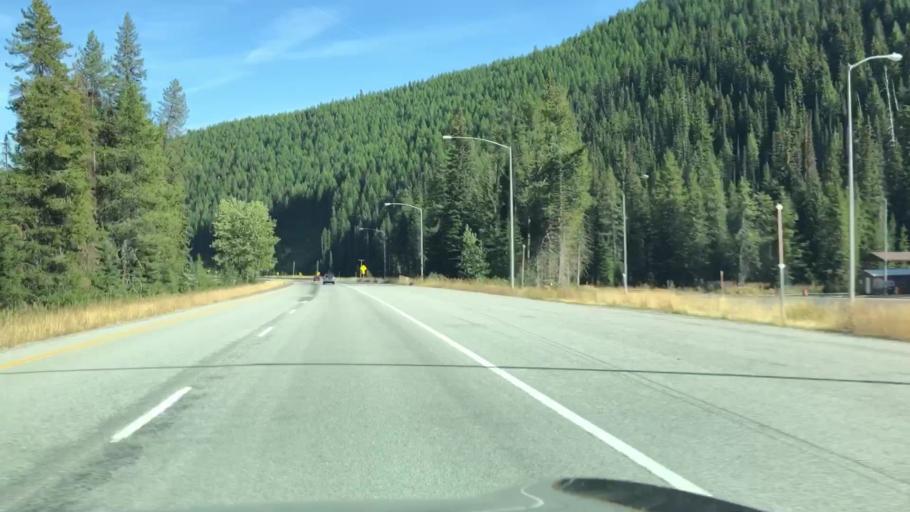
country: US
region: Idaho
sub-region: Shoshone County
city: Wallace
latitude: 47.4200
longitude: -115.6286
